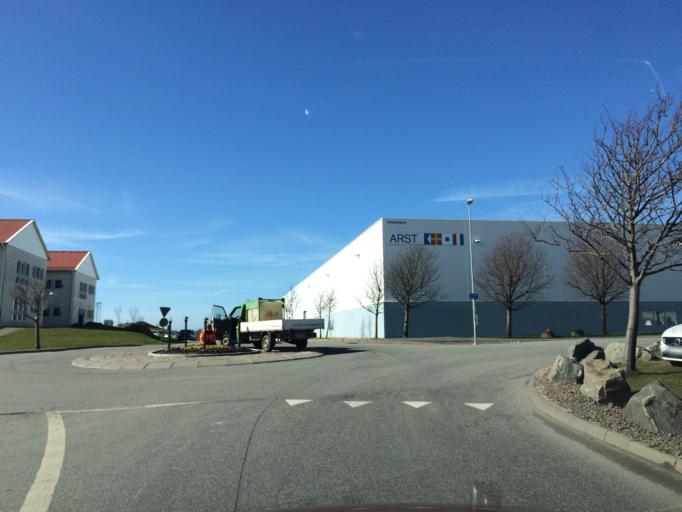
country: SE
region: Vaestra Goetaland
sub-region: Goteborg
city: Torslanda
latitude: 57.6977
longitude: 11.8104
